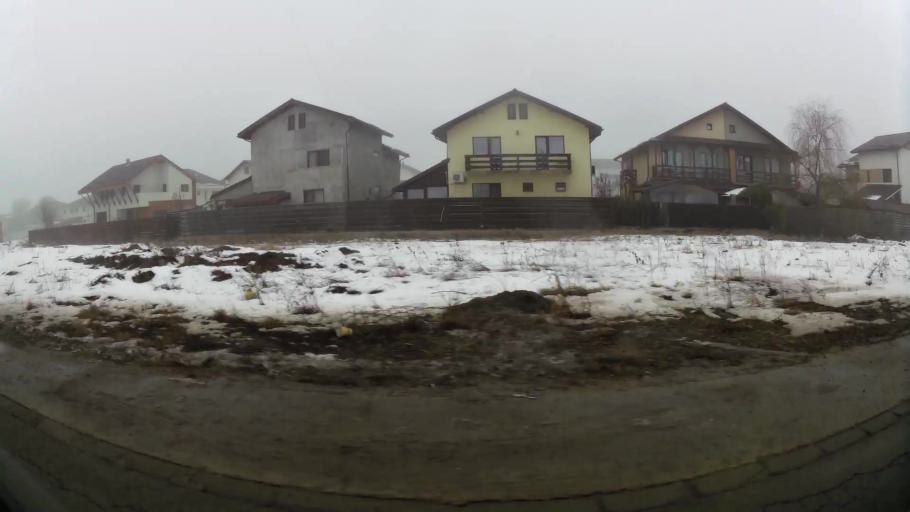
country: RO
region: Ilfov
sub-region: Comuna Chiajna
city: Chiajna
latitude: 44.4505
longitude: 25.9799
